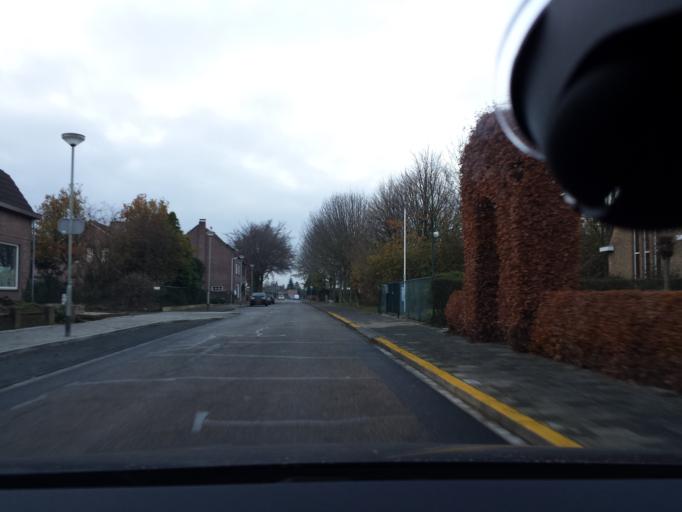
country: NL
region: Limburg
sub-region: Gemeente Kerkrade
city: Kerkrade
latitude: 50.9188
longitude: 6.0406
